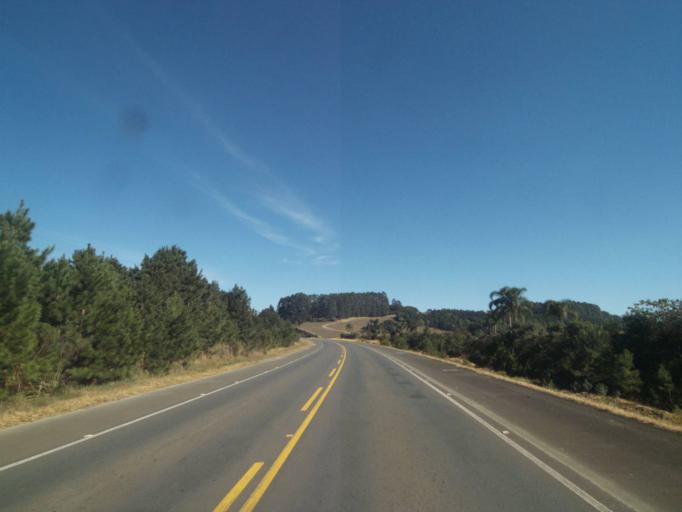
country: BR
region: Parana
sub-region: Tibagi
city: Tibagi
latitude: -24.8085
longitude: -50.4787
